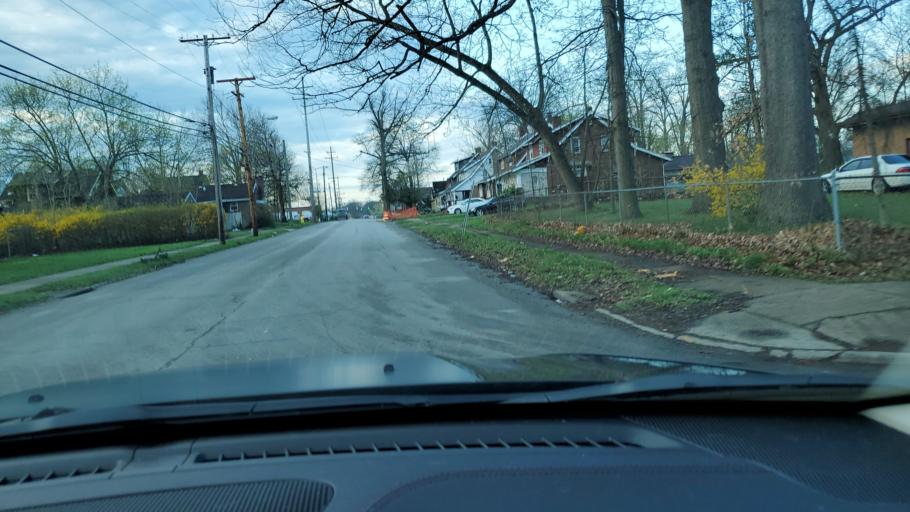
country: US
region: Ohio
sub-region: Mahoning County
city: Youngstown
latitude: 41.0636
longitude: -80.6640
